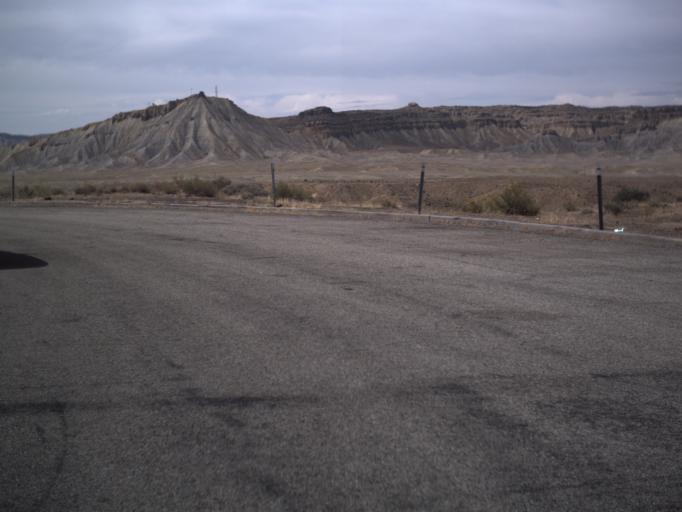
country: US
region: Utah
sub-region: Grand County
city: Moab
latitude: 38.9386
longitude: -109.8277
